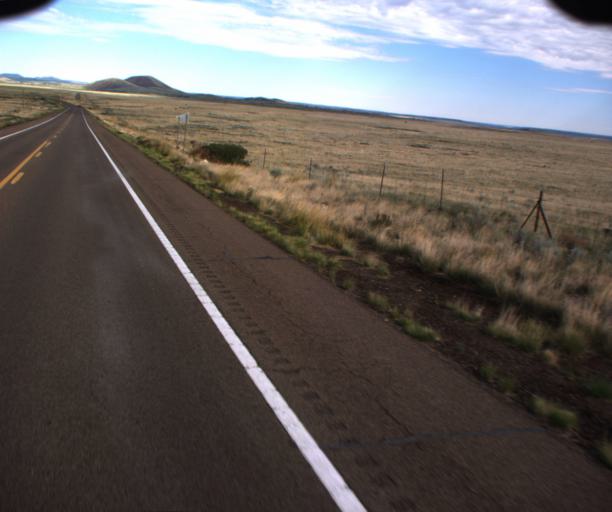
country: US
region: Arizona
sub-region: Apache County
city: Springerville
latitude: 34.1828
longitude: -109.3295
